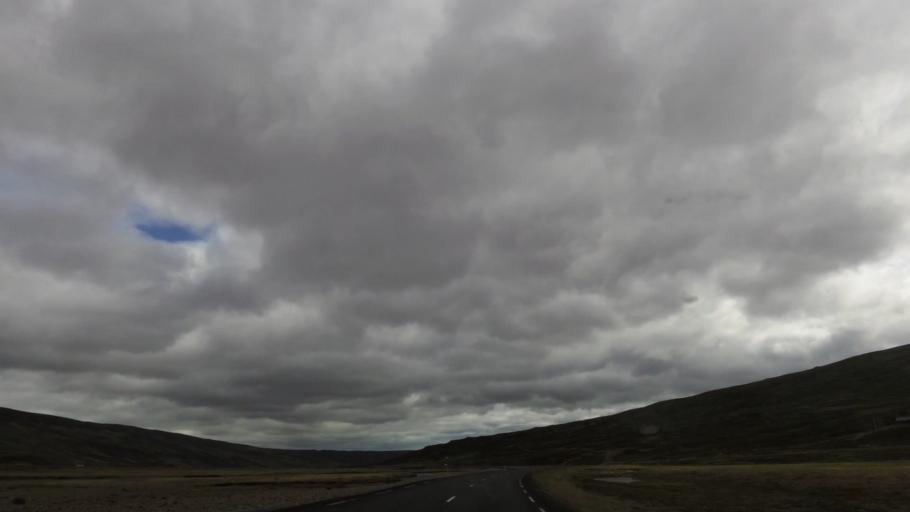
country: IS
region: West
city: Stykkisholmur
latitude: 65.7583
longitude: -21.8725
